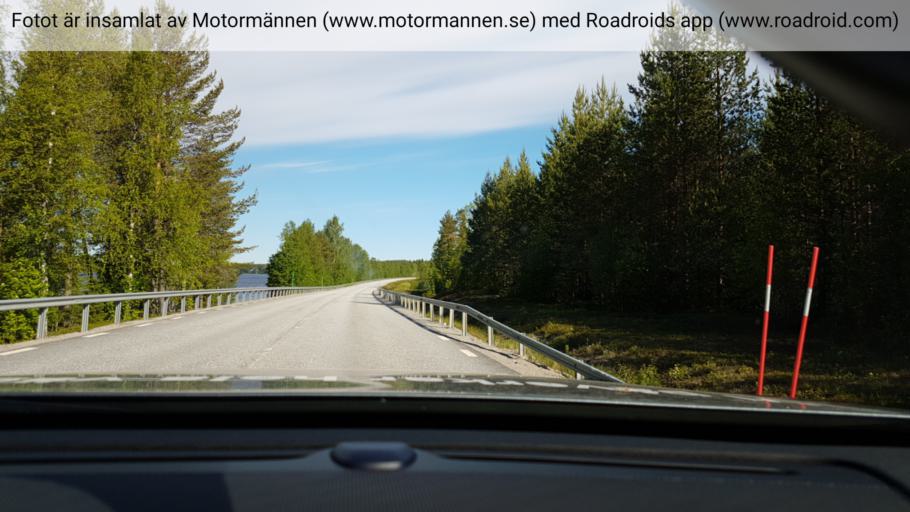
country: SE
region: Vaesterbotten
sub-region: Vindelns Kommun
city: Vindeln
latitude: 64.1860
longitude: 19.4695
